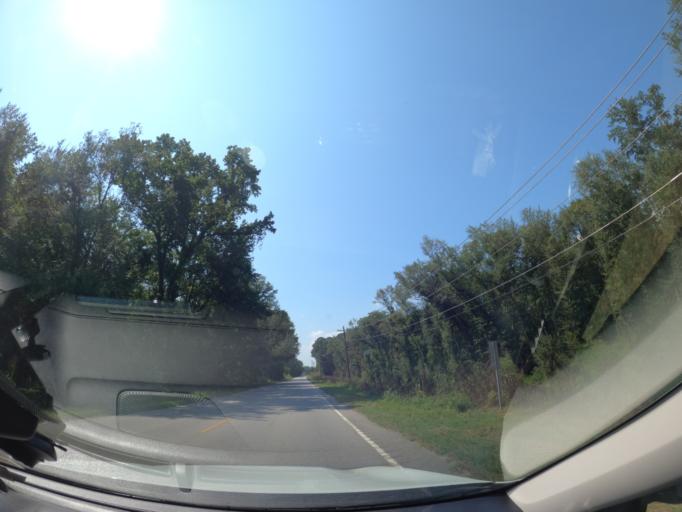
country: US
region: South Carolina
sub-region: Richland County
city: Hopkins
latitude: 33.9234
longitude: -80.9576
